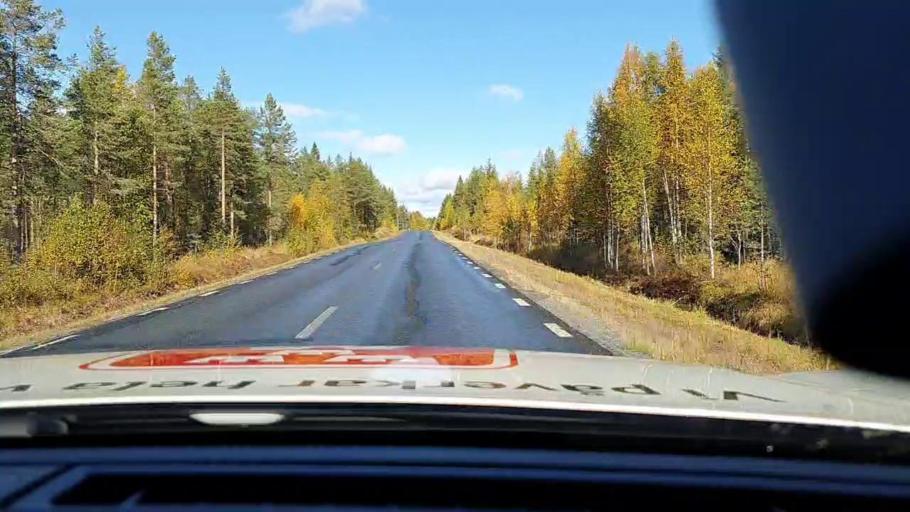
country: SE
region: Vaesterbotten
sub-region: Skelleftea Kommun
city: Langsele
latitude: 64.9959
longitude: 20.0901
